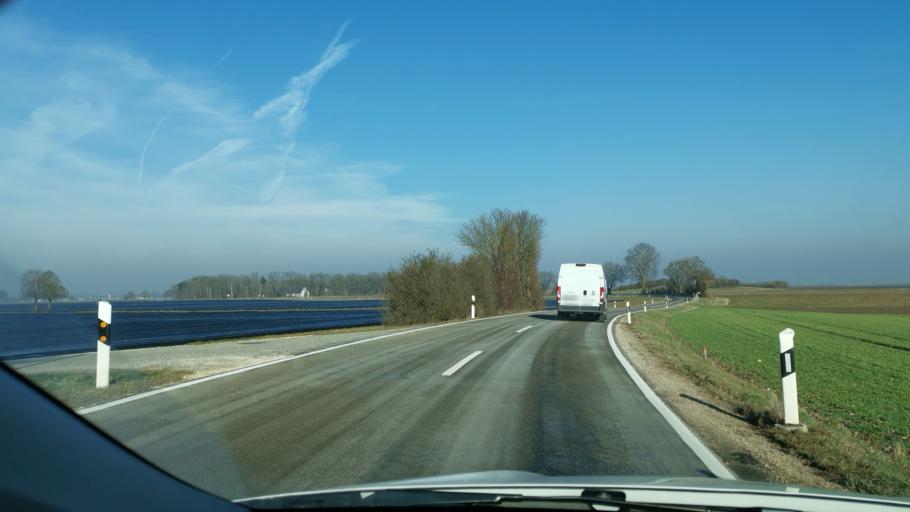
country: DE
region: Bavaria
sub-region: Swabia
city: Munster
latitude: 48.6346
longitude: 10.9253
